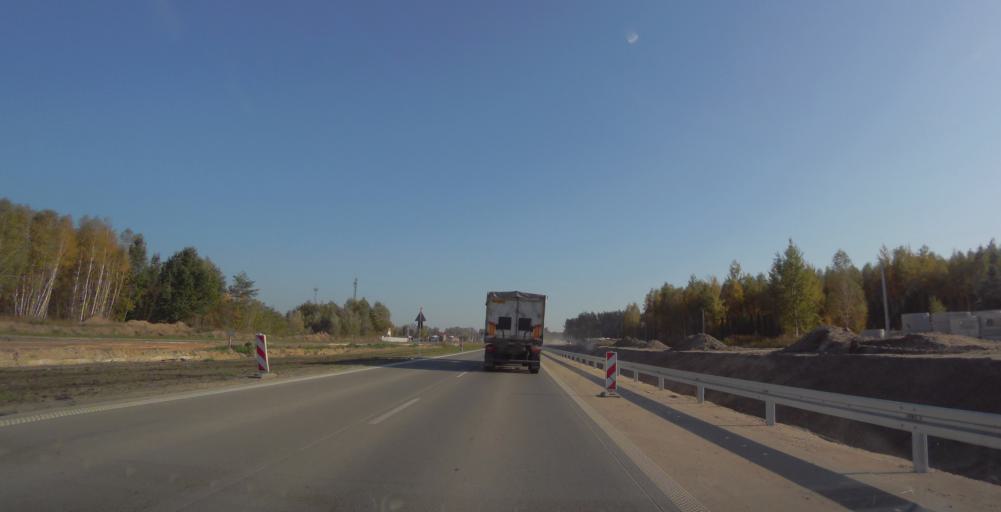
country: PL
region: Masovian Voivodeship
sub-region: Powiat otwocki
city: Celestynow
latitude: 52.1173
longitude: 21.3698
